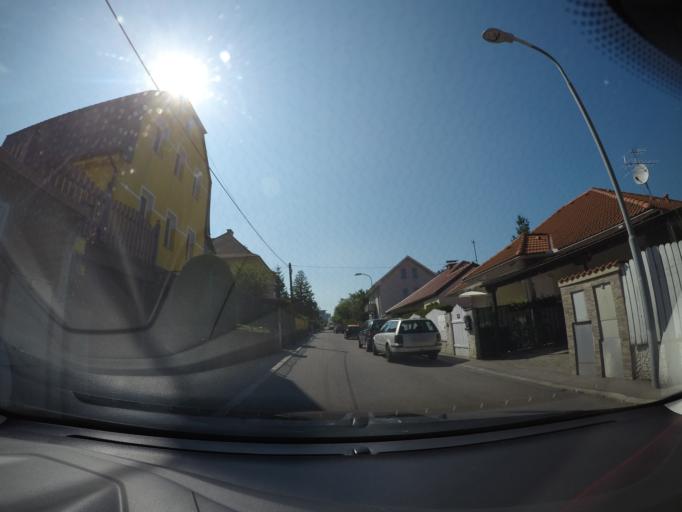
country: AT
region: Lower Austria
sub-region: Politischer Bezirk Modling
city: Perchtoldsdorf
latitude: 48.1641
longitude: 16.2650
